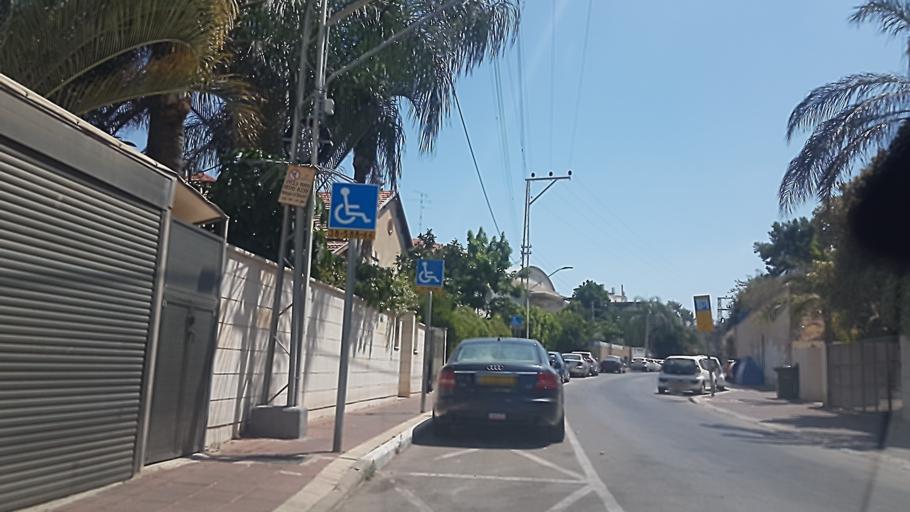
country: IL
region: Tel Aviv
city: Bene Beraq
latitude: 32.0829
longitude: 34.8237
